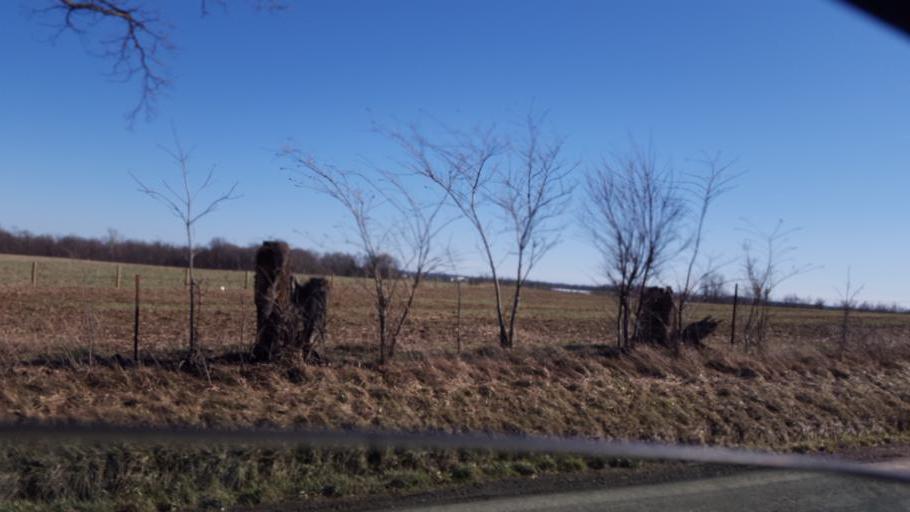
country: US
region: Ohio
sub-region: Wayne County
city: Apple Creek
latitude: 40.6584
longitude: -81.7556
